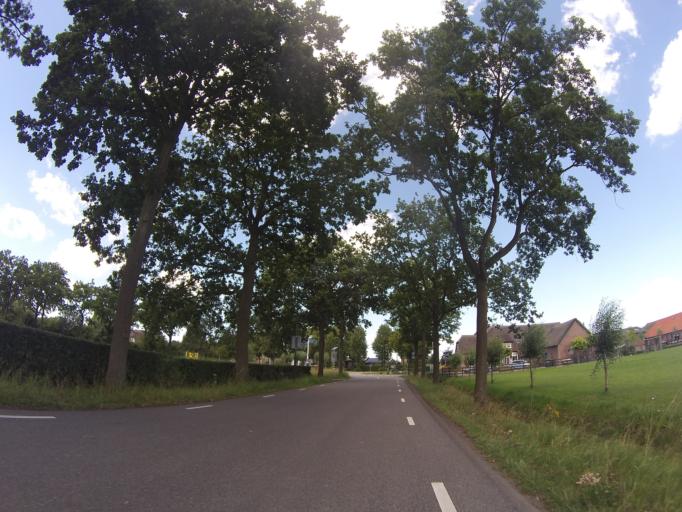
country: NL
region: Utrecht
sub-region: Stichtse Vecht
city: Spechtenkamp
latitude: 52.1317
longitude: 4.9859
